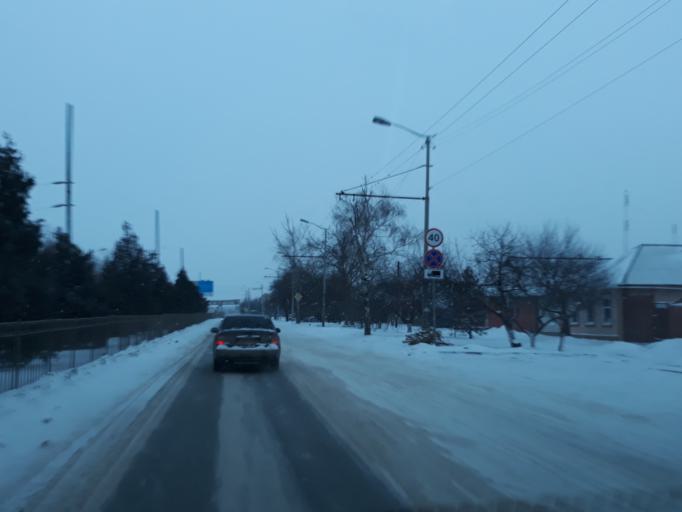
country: RU
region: Rostov
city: Taganrog
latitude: 47.2700
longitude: 38.9214
